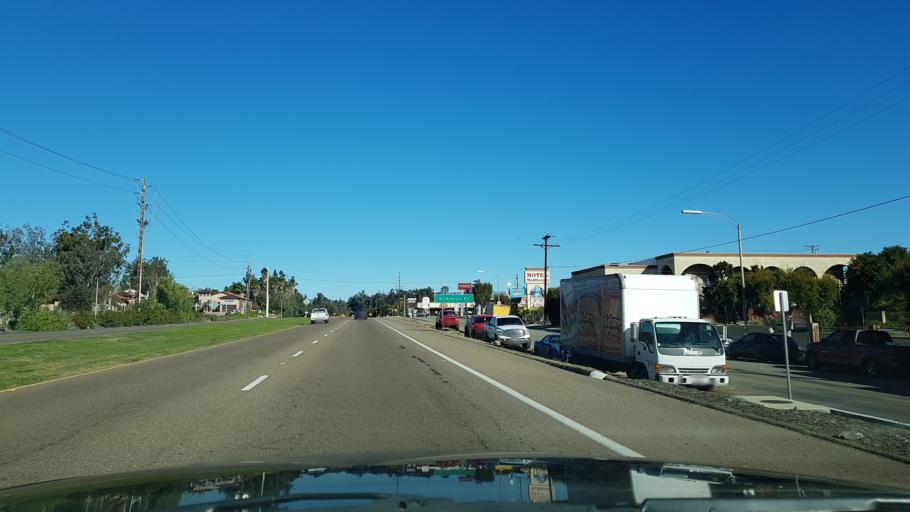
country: US
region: California
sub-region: San Diego County
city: Escondido
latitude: 33.0919
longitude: -117.0723
